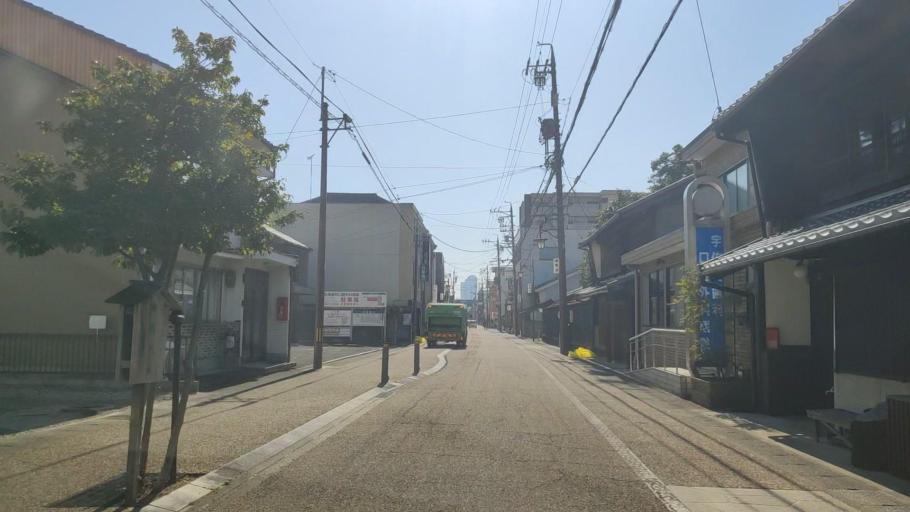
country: JP
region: Gifu
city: Gifu-shi
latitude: 35.4304
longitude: 136.7670
